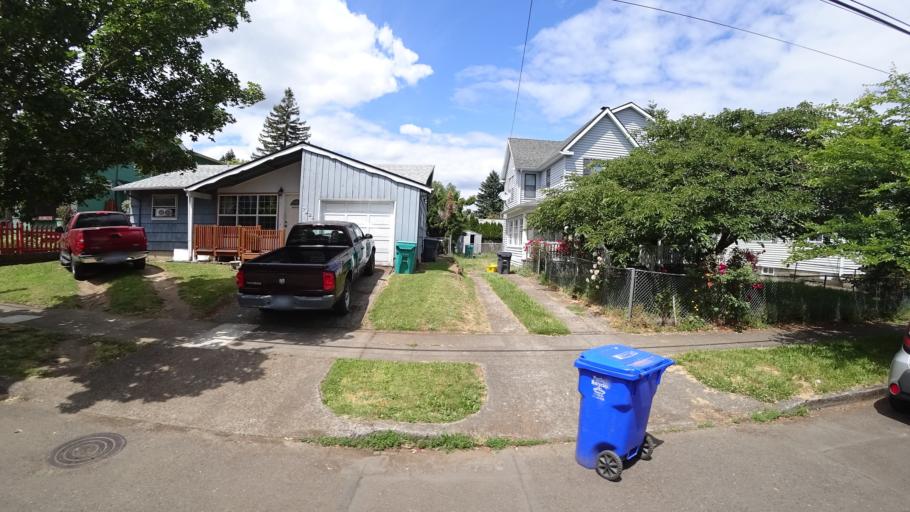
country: US
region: Oregon
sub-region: Multnomah County
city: Portland
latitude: 45.5846
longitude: -122.7254
